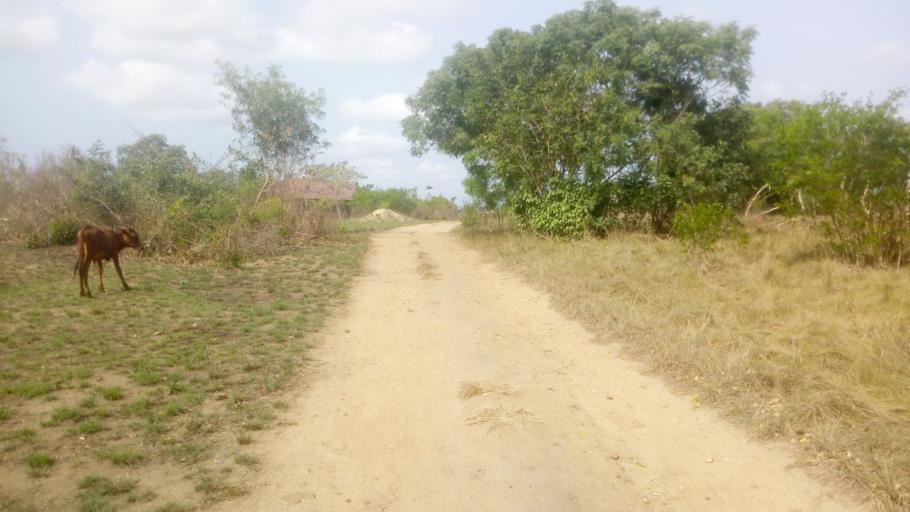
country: GH
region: Central
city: Winneba
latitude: 5.3792
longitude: -0.6270
